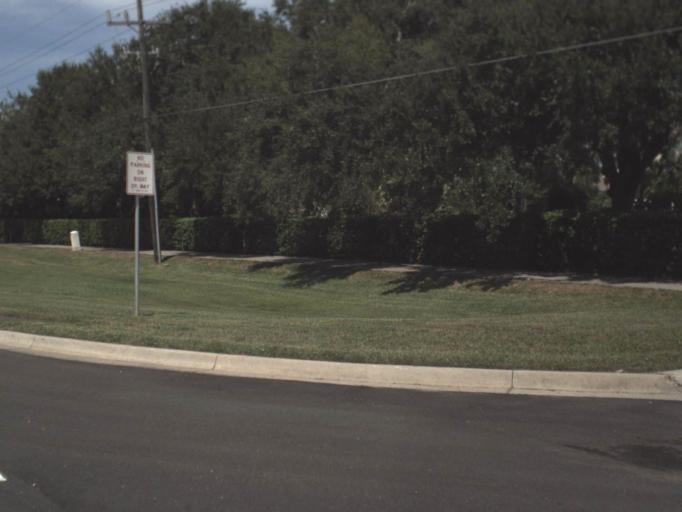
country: US
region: Florida
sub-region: Manatee County
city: Cortez
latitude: 27.4963
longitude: -82.6711
